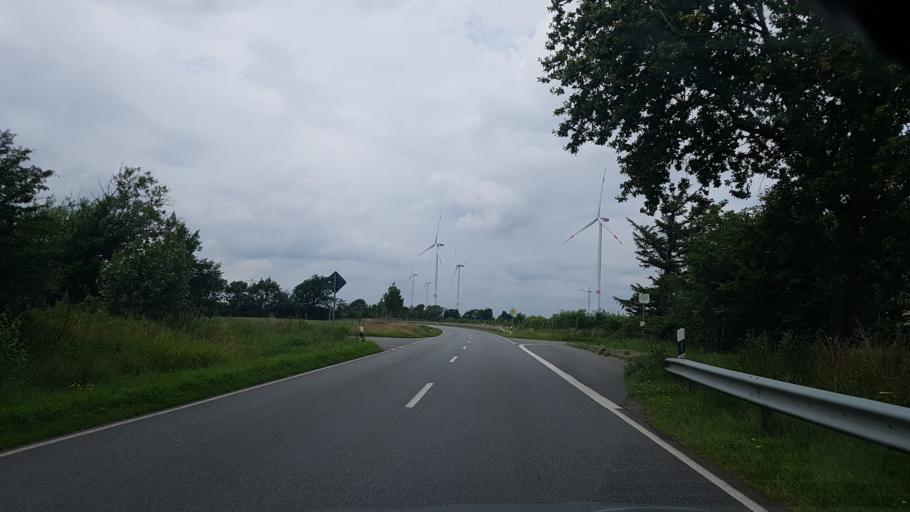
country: DE
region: Schleswig-Holstein
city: Jardelund
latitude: 54.8404
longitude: 9.2105
